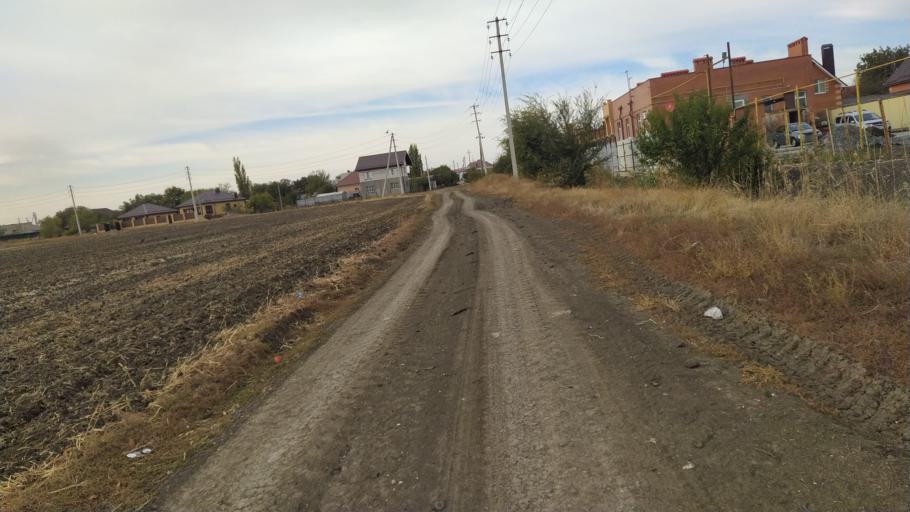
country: RU
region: Rostov
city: Bataysk
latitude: 47.1121
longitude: 39.6799
